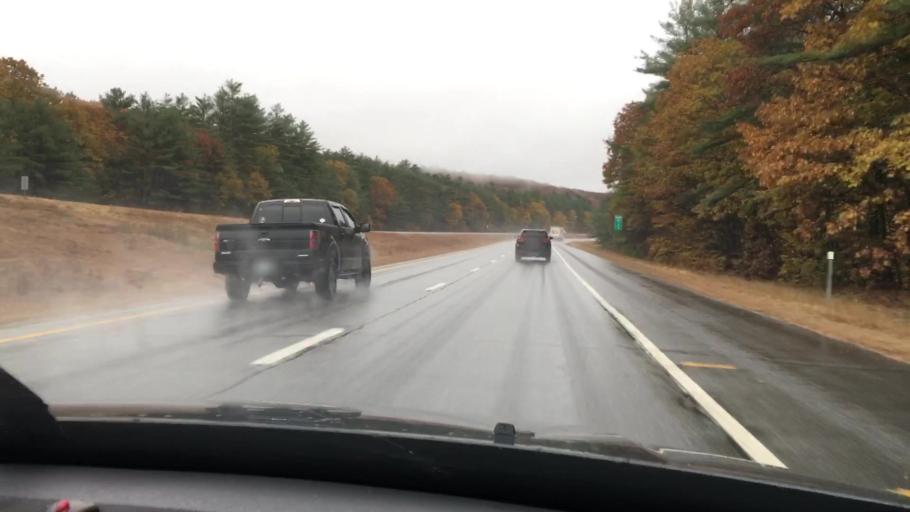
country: US
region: New Hampshire
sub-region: Grafton County
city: Ashland
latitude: 43.6492
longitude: -71.6479
